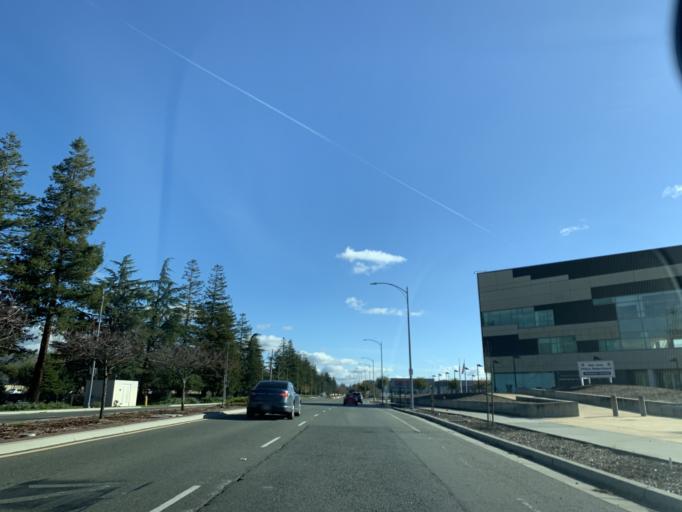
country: US
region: California
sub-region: Santa Clara County
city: Seven Trees
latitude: 37.2464
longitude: -121.7885
